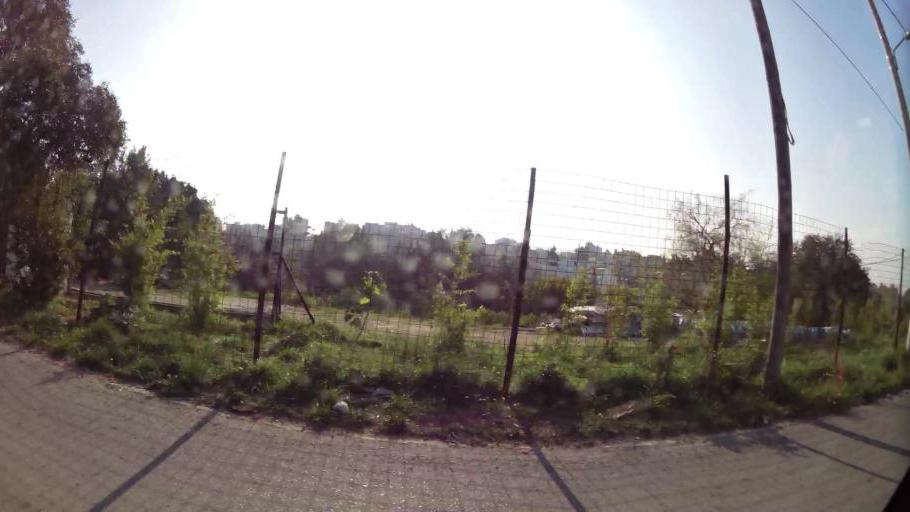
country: GR
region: Attica
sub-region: Nomarchia Athinas
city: Nea Filadelfeia
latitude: 38.0537
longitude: 23.7393
